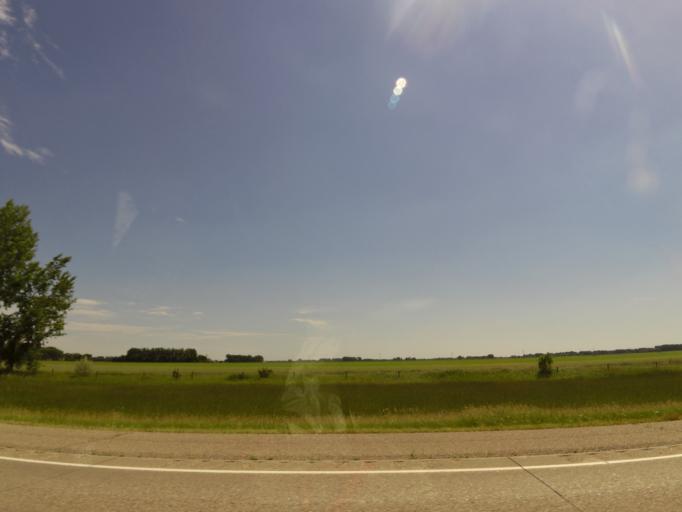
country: US
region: North Dakota
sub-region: Grand Forks County
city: Grand Forks
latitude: 47.8124
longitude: -97.0776
